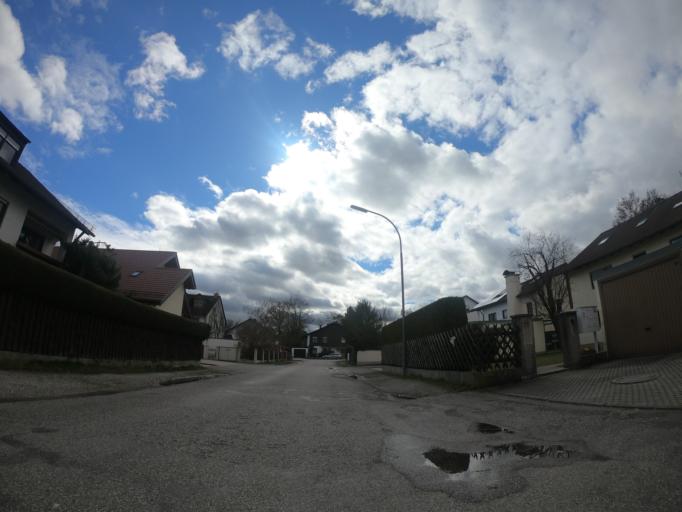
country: DE
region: Bavaria
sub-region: Upper Bavaria
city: Fuerstenfeldbruck
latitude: 48.1669
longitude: 11.2320
